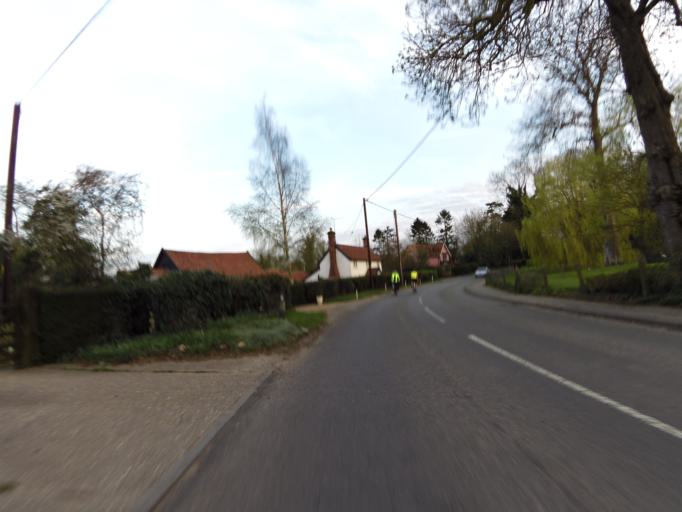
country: GB
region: England
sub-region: Suffolk
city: Debenham
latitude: 52.1499
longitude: 1.2217
